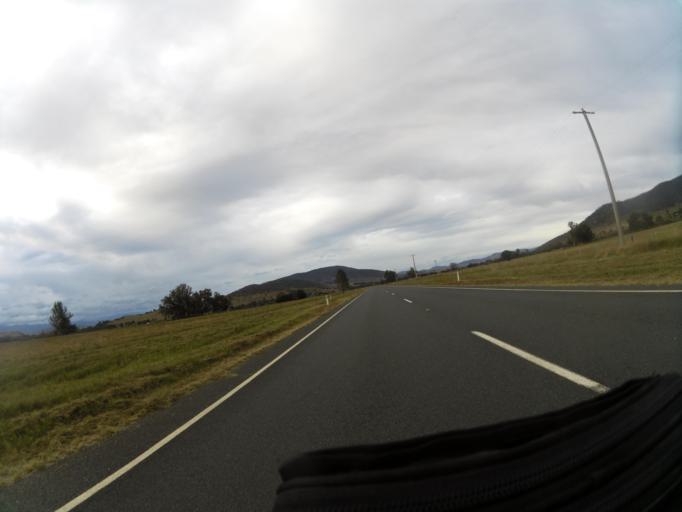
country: AU
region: New South Wales
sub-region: Snowy River
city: Jindabyne
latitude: -36.1100
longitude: 147.9795
